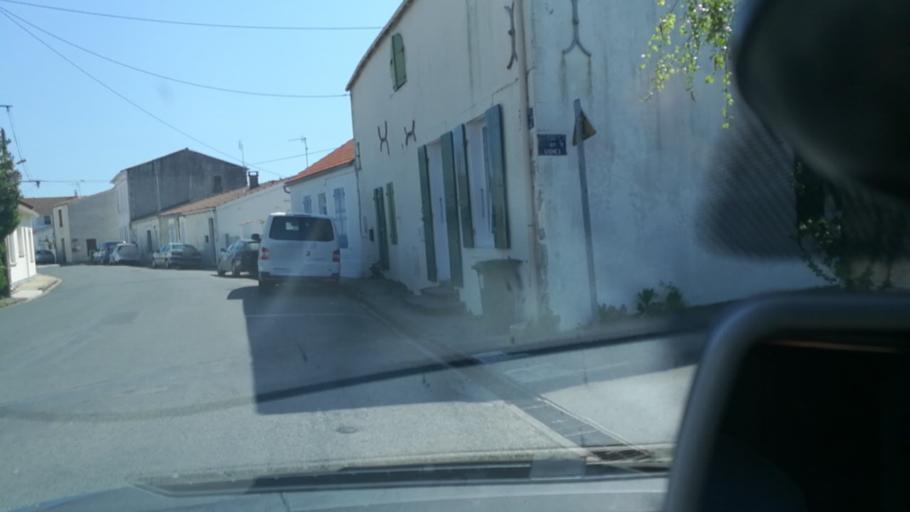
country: FR
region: Poitou-Charentes
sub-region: Departement de la Charente-Maritime
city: Saint-Trojan-les-Bains
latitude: 45.8729
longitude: -1.2087
